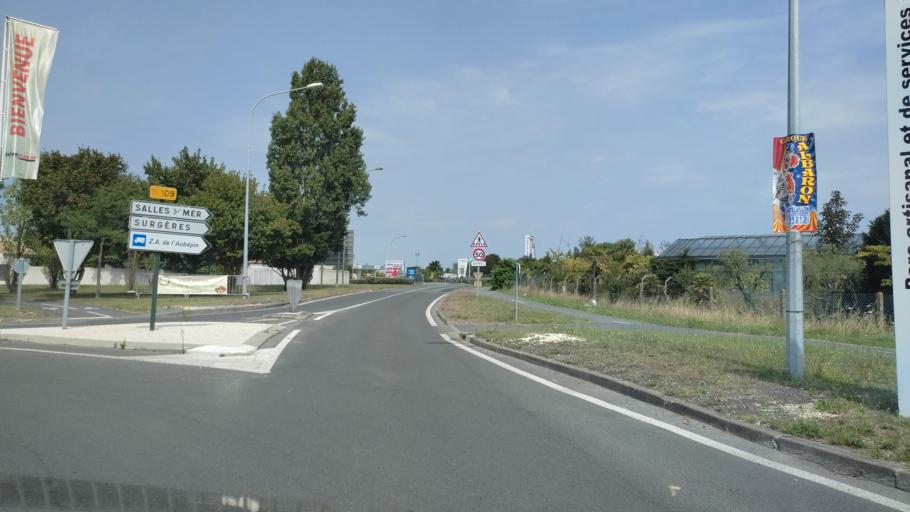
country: FR
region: Poitou-Charentes
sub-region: Departement de la Charente-Maritime
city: Chatelaillon-Plage
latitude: 46.0828
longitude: -1.0750
